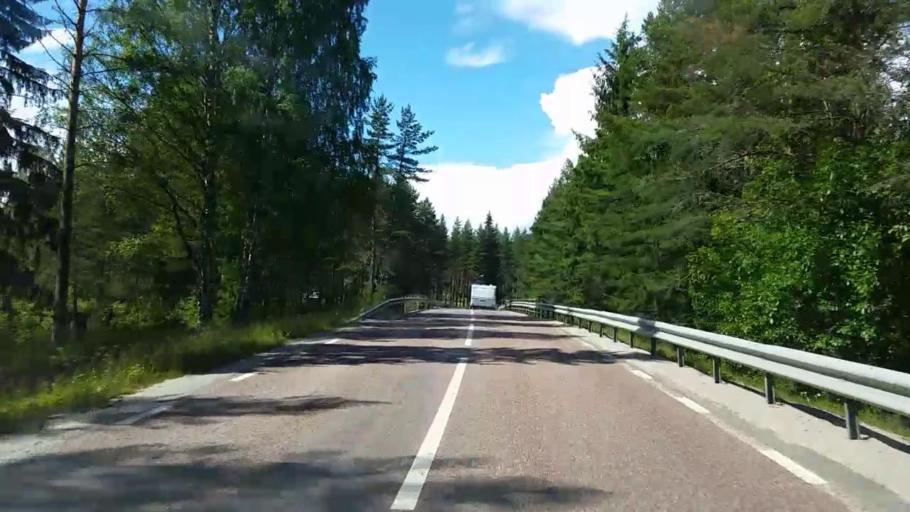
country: SE
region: Gaevleborg
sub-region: Ovanakers Kommun
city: Edsbyn
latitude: 61.3069
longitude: 15.5086
